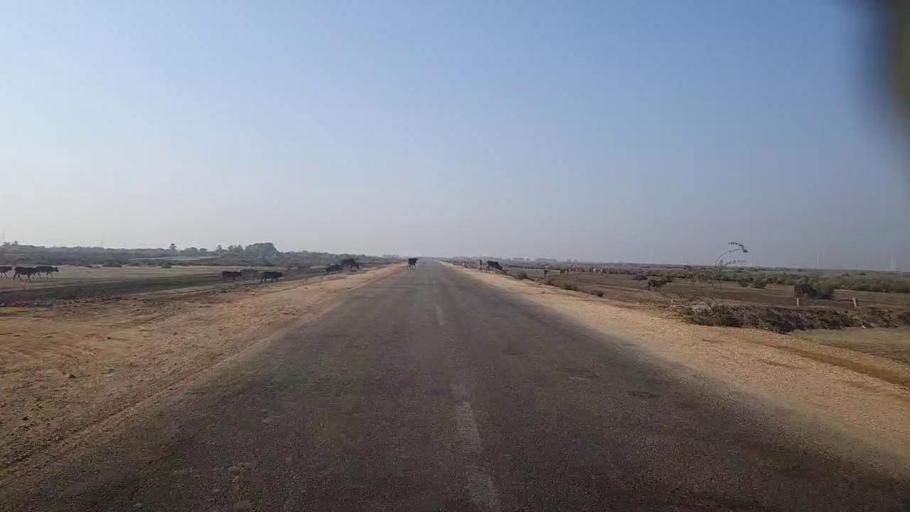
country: PK
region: Sindh
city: Gharo
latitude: 24.6988
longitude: 67.5267
